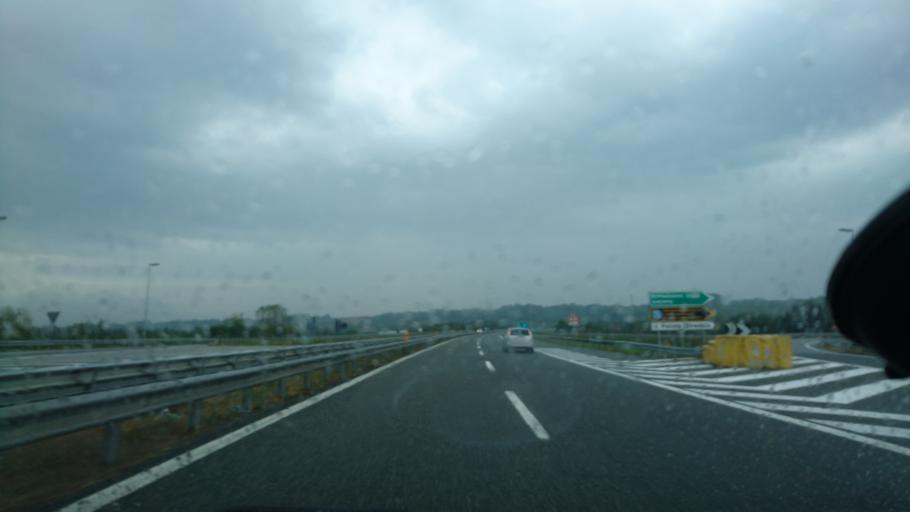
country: IT
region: Piedmont
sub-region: Provincia di Novara
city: Ghemme
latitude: 45.6059
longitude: 8.4052
